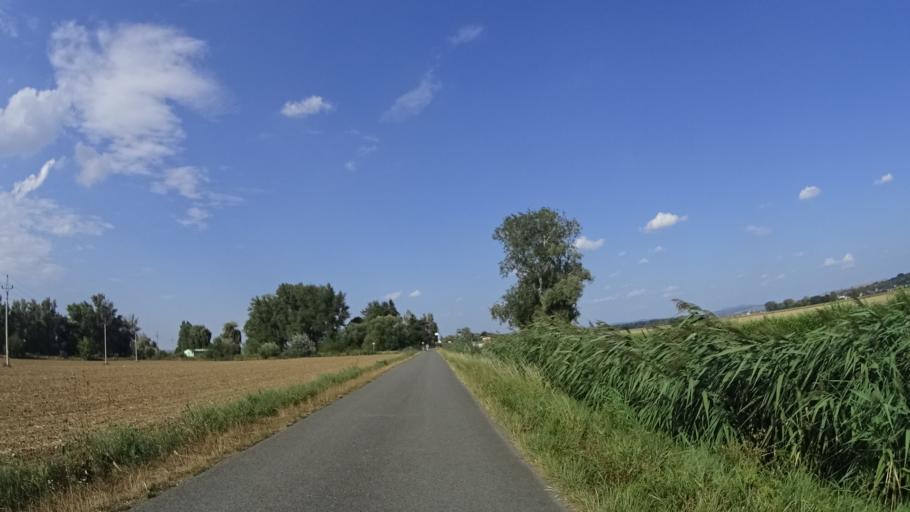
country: CZ
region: Zlin
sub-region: Okres Uherske Hradiste
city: Uherske Hradiste
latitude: 49.0831
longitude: 17.4649
